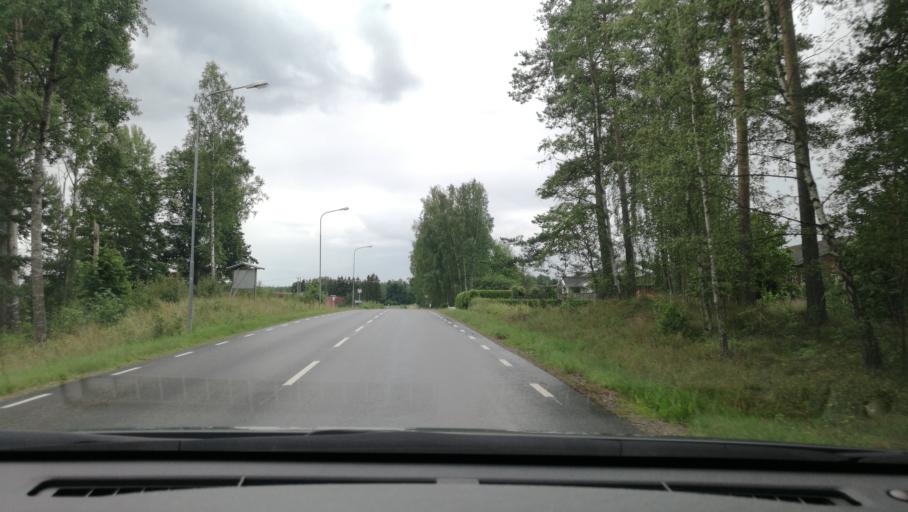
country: SE
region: OEstergoetland
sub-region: Norrkopings Kommun
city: Svartinge
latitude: 58.8250
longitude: 15.9418
